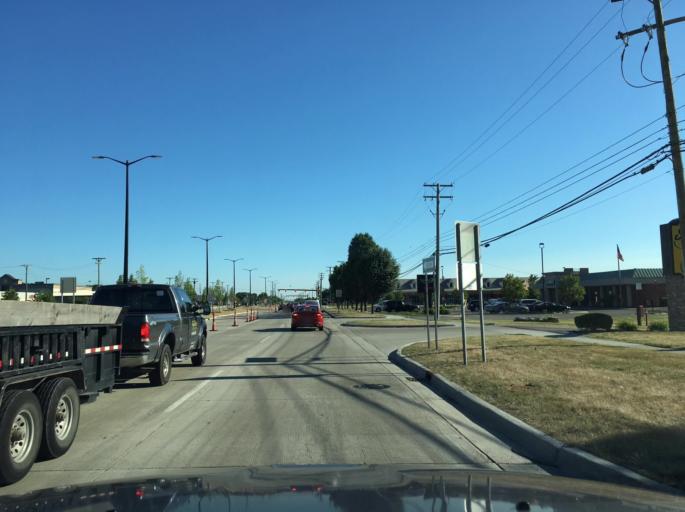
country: US
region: Michigan
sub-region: Macomb County
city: Sterling Heights
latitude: 42.5477
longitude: -83.0287
